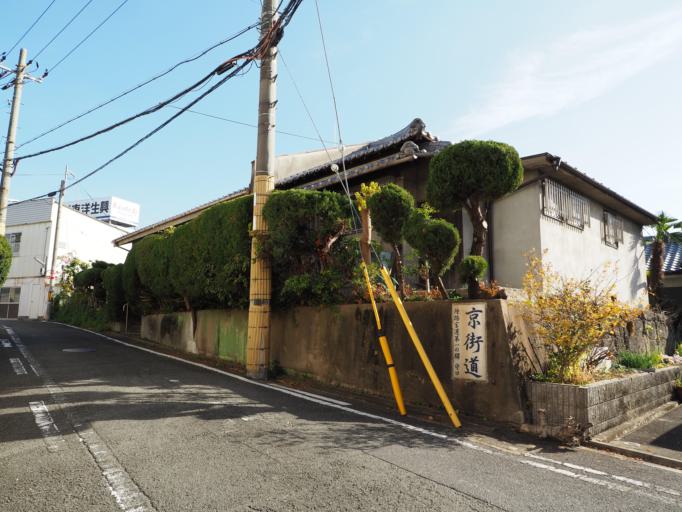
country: JP
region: Osaka
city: Moriguchi
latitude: 34.7346
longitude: 135.5622
